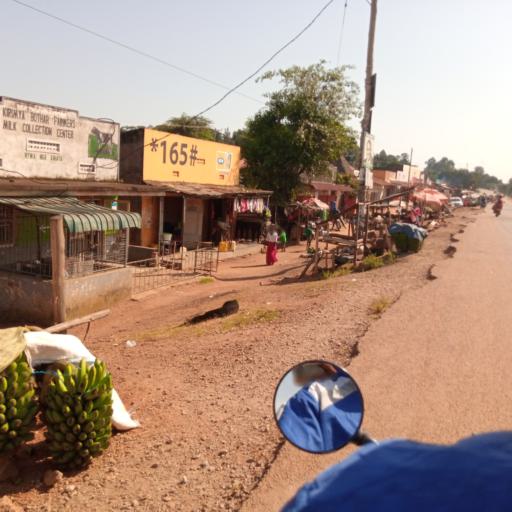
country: UG
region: Central Region
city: Masaka
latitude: -0.3750
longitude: 31.7145
